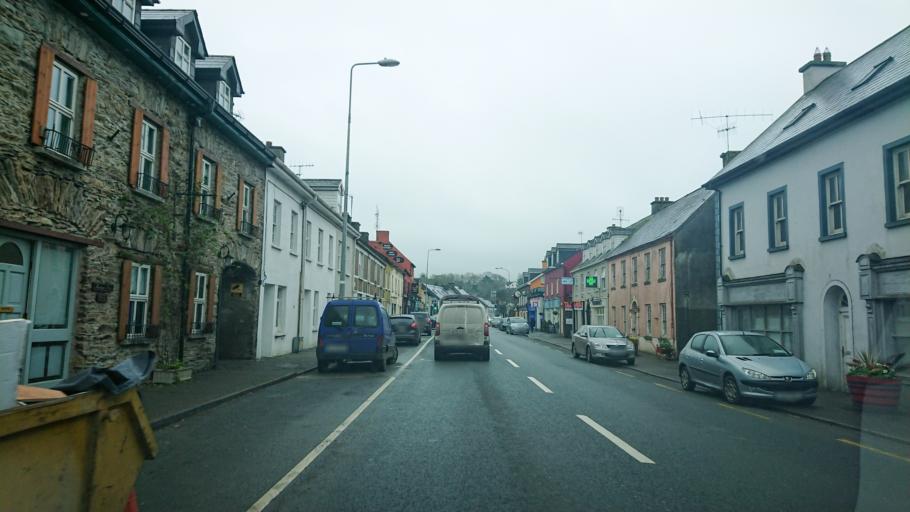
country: IE
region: Munster
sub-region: County Cork
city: Bandon
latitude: 51.7651
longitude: -8.6590
